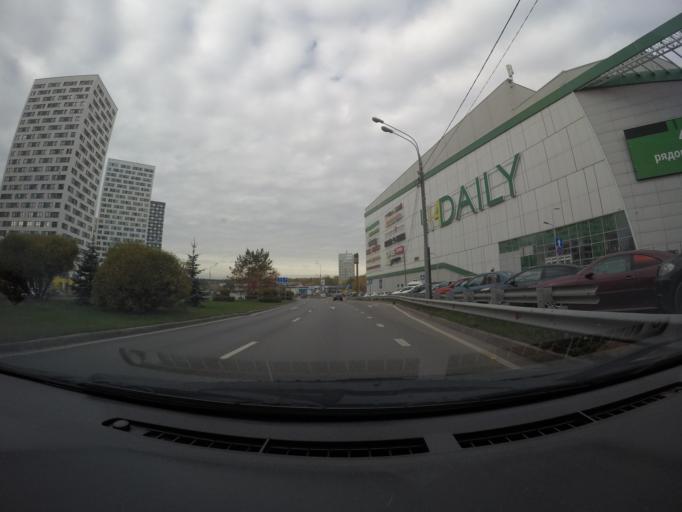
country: RU
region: Moskovskaya
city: Mytishchi
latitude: 55.9213
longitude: 37.7179
